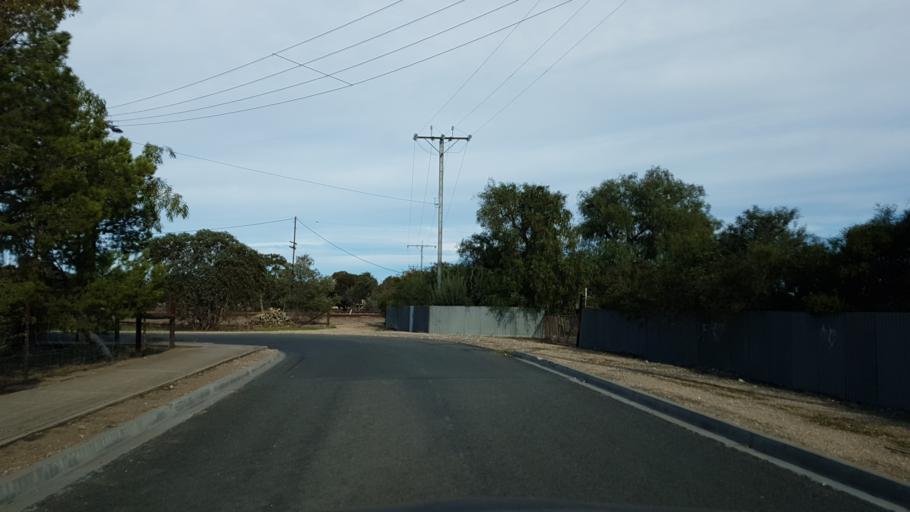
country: AU
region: South Australia
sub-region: Murray Bridge
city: Tailem Bend
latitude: -35.2509
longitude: 139.4536
